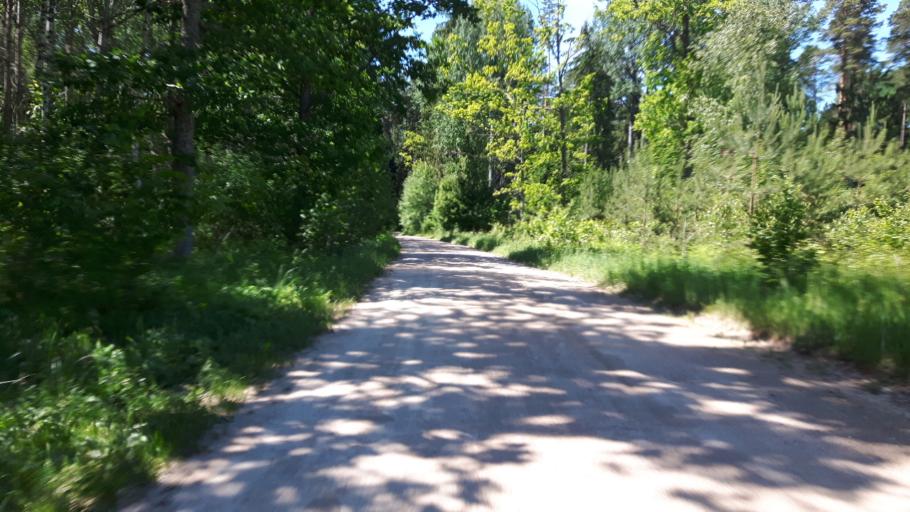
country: LV
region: Kandava
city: Kandava
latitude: 57.0427
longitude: 22.8478
